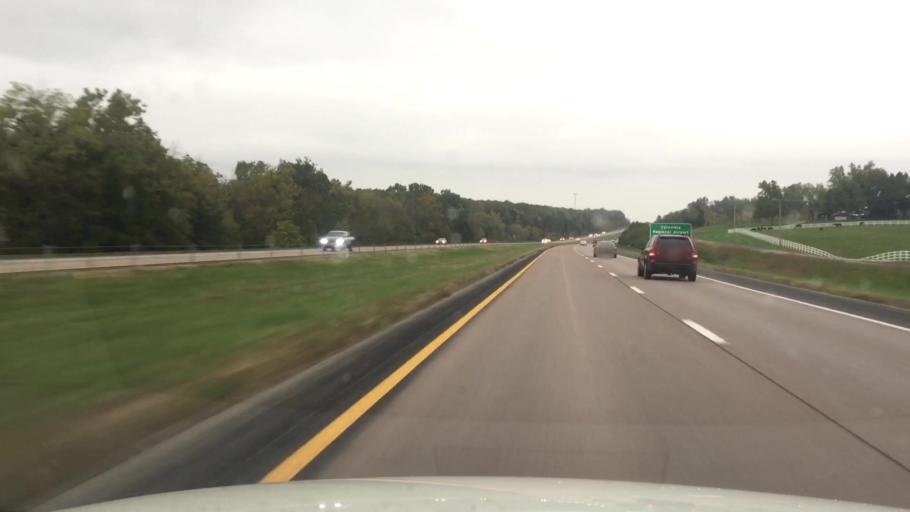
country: US
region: Missouri
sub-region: Boone County
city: Ashland
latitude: 38.8180
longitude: -92.2513
